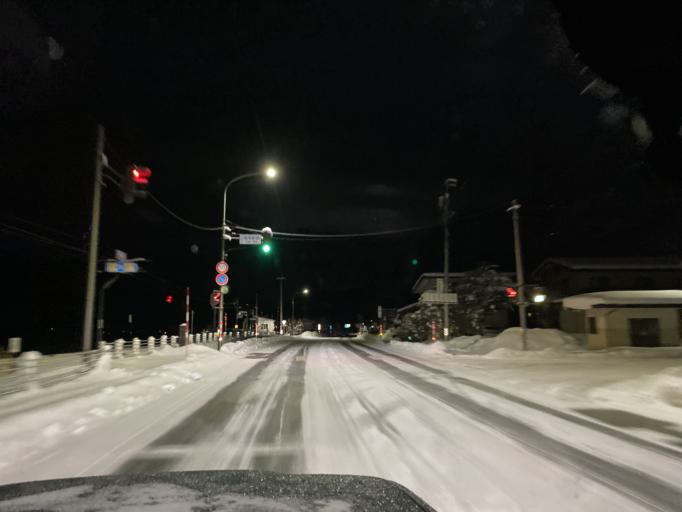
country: JP
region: Nagano
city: Omachi
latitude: 36.5532
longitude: 137.8427
